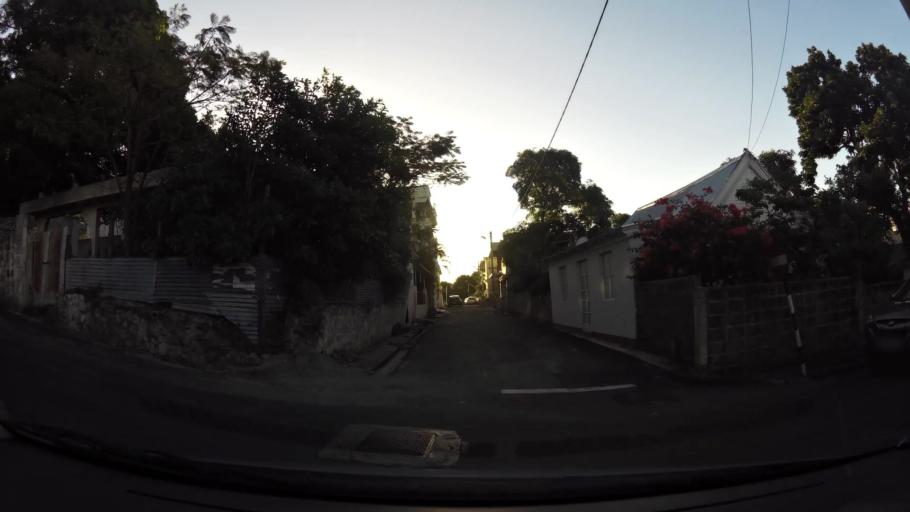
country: MU
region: Port Louis
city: Port Louis
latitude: -20.1703
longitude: 57.4981
